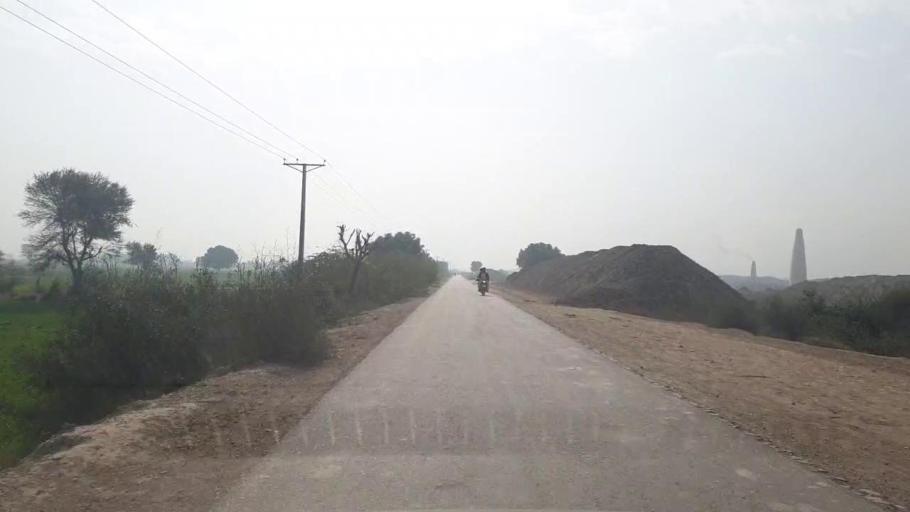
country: PK
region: Sindh
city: Hala
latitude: 25.7705
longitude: 68.4460
